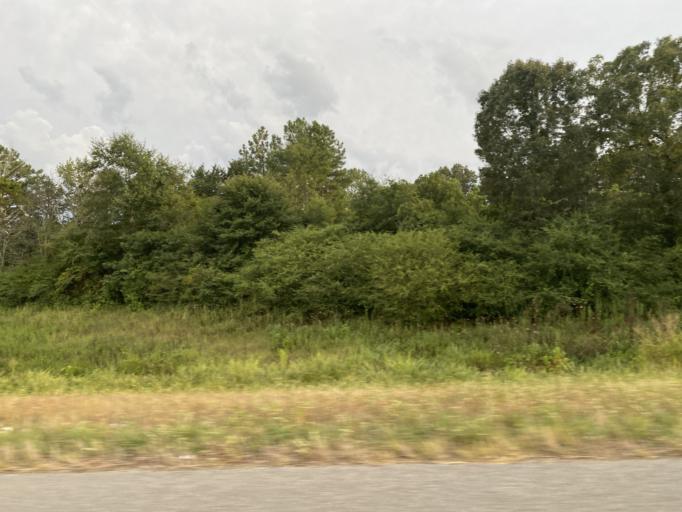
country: US
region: Alabama
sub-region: Franklin County
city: Red Bay
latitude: 34.4492
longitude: -88.0598
